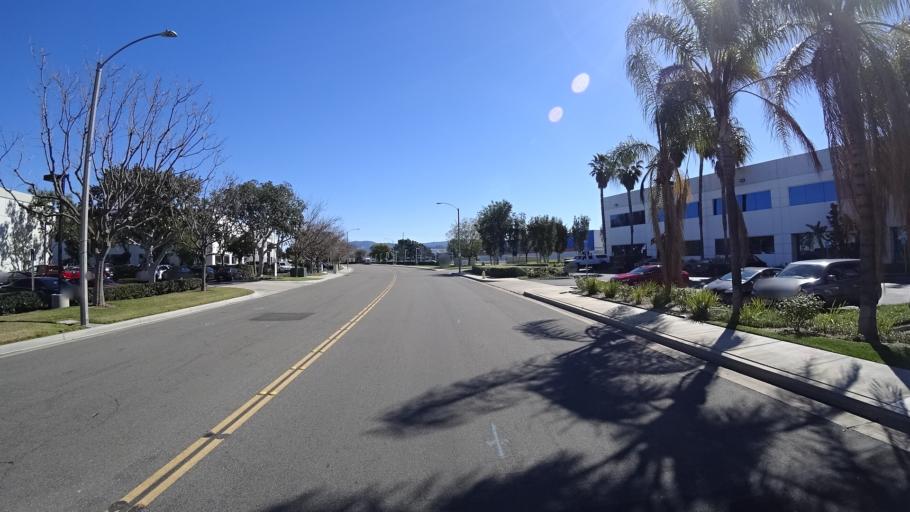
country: US
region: California
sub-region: Orange County
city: Yorba Linda
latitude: 33.8620
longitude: -117.8092
